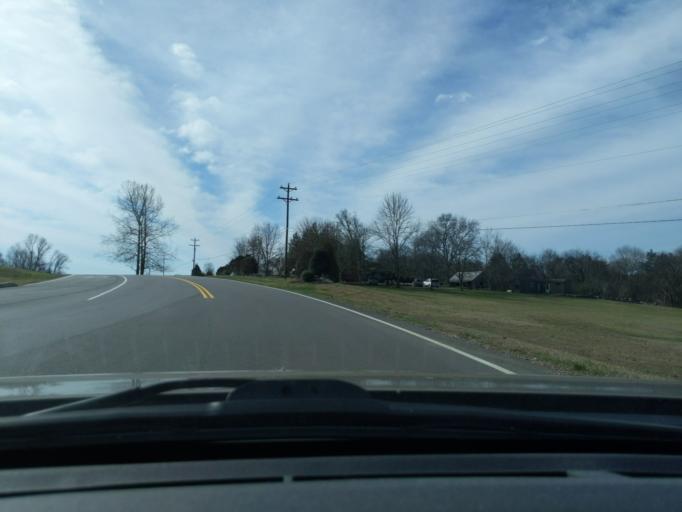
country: US
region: Tennessee
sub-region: Wilson County
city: Mount Juliet
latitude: 36.2171
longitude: -86.4954
